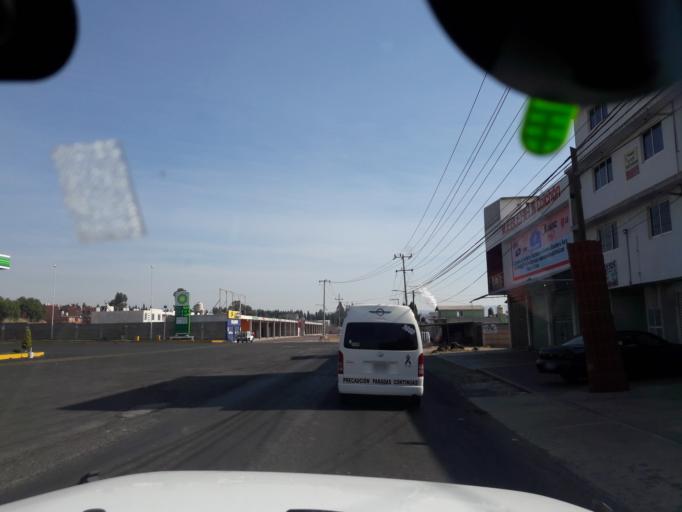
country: MX
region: Tlaxcala
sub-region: Ixtacuixtla de Mariano Matamoros
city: Villa Mariano Matamoros
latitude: 19.2984
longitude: -98.3991
